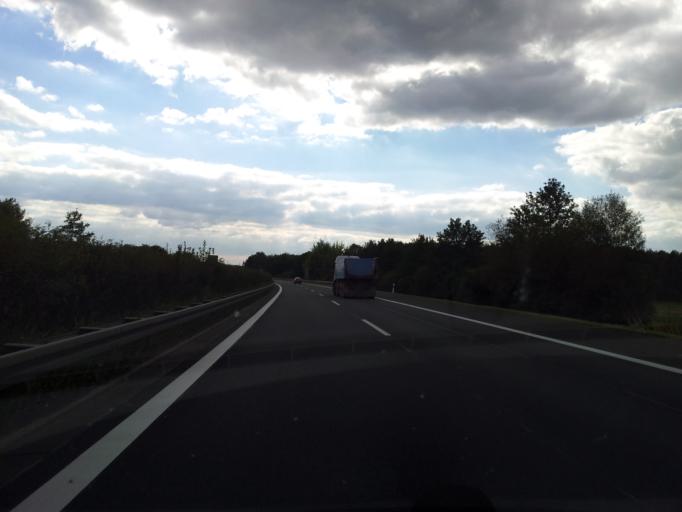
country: DE
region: Brandenburg
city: Schipkau
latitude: 51.5537
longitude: 13.9133
